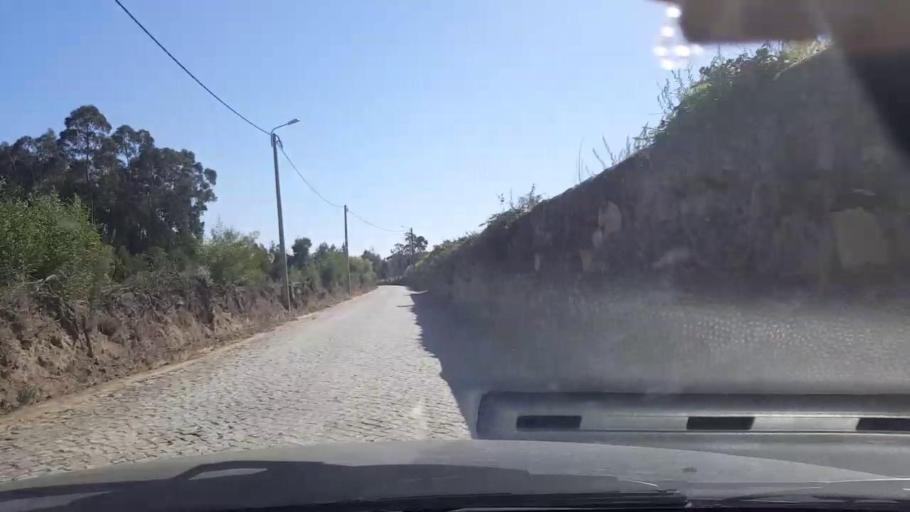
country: PT
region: Porto
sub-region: Vila do Conde
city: Arvore
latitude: 41.3149
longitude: -8.6879
